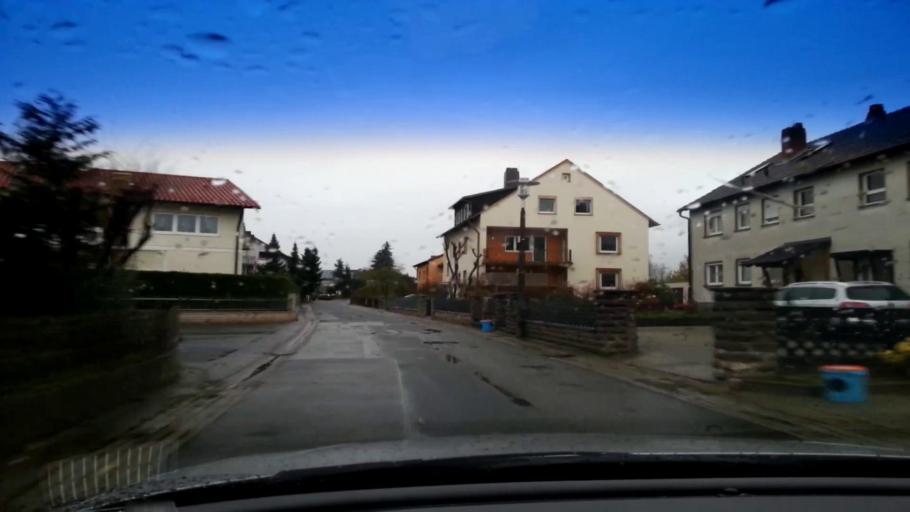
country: DE
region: Bavaria
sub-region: Upper Franconia
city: Hallstadt
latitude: 49.9245
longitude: 10.8843
